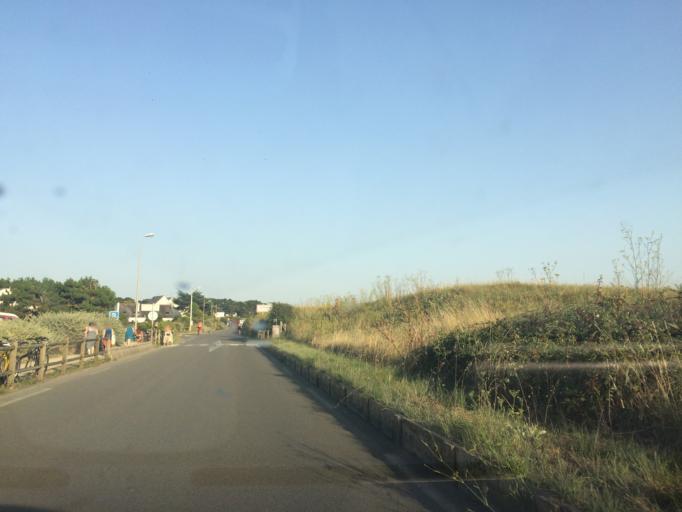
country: FR
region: Brittany
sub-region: Departement du Morbihan
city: Damgan
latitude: 47.5142
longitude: -2.5595
